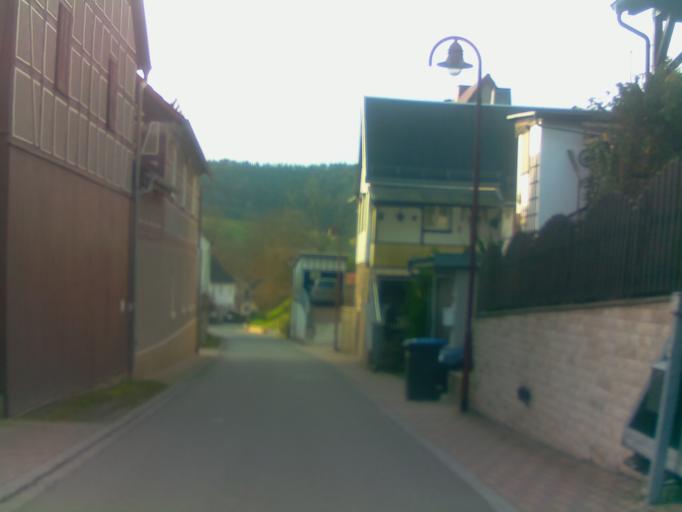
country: DE
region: Thuringia
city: Hummelshain
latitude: 50.7473
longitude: 11.6393
